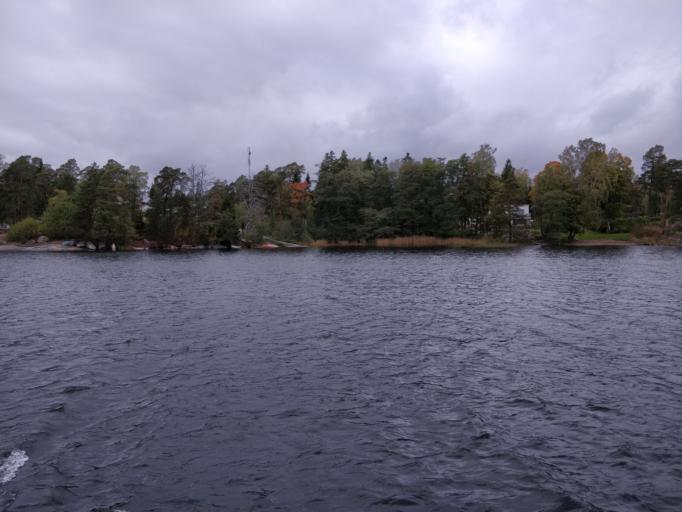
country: FI
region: Uusimaa
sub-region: Helsinki
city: Vantaa
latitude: 60.1601
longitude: 25.0982
